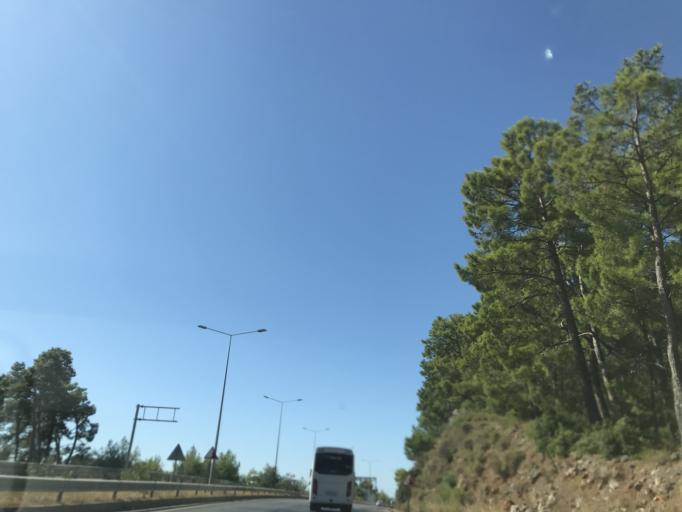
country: TR
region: Antalya
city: Cakirlar
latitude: 36.7601
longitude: 30.5694
